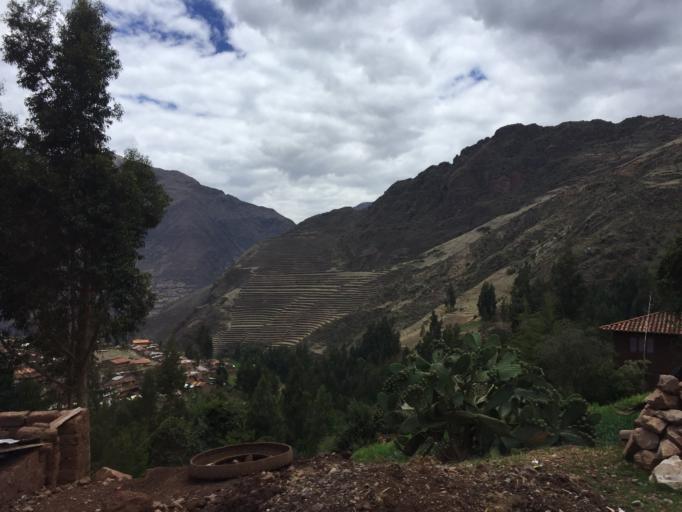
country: PE
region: Cusco
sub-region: Provincia de Calca
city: Pisac
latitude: -13.4068
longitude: -71.8336
